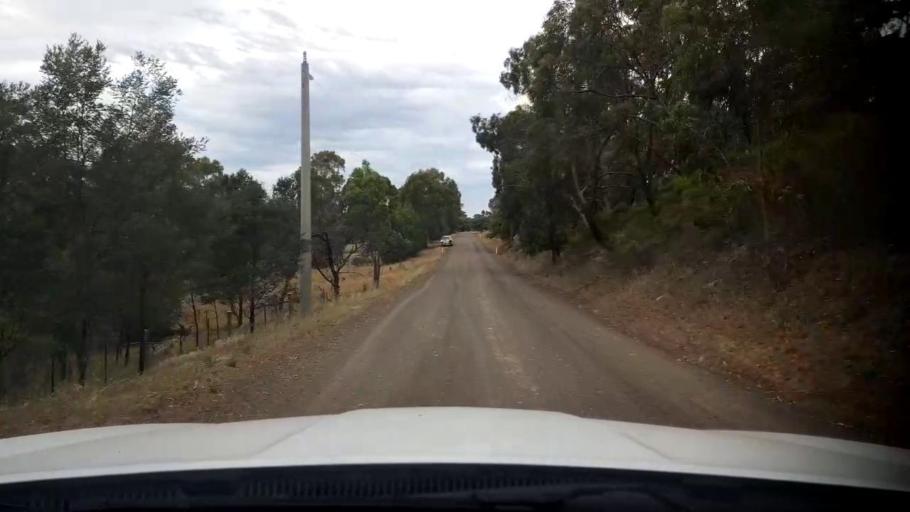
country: AU
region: Victoria
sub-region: Whittlesea
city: Whittlesea
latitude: -37.4872
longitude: 145.0630
